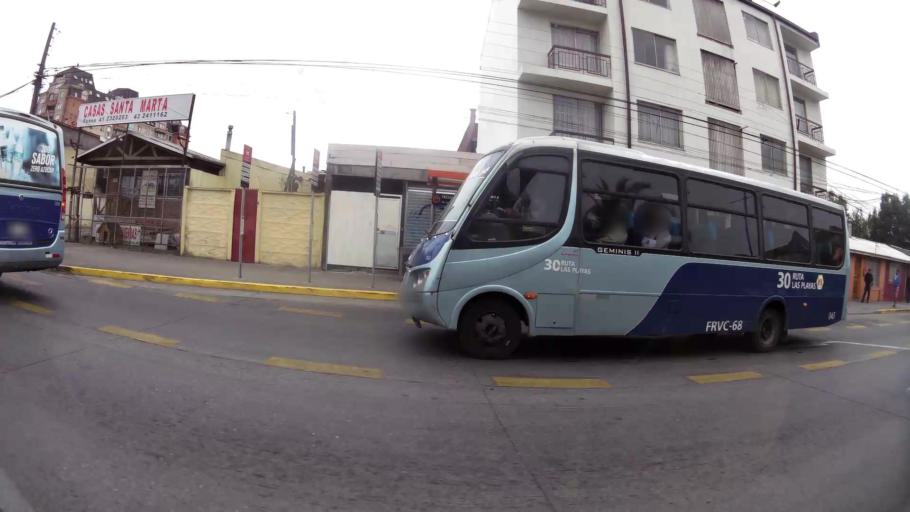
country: CL
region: Biobio
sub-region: Provincia de Concepcion
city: Concepcion
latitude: -36.8158
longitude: -73.0340
